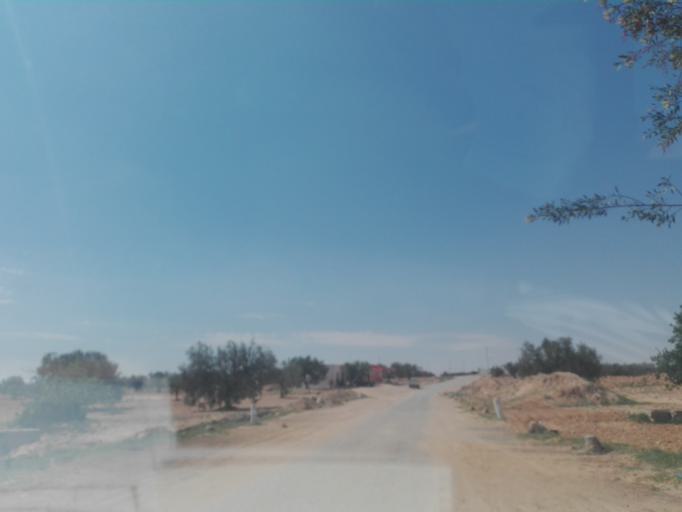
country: TN
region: Safaqis
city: Bi'r `Ali Bin Khalifah
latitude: 34.6171
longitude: 10.3615
